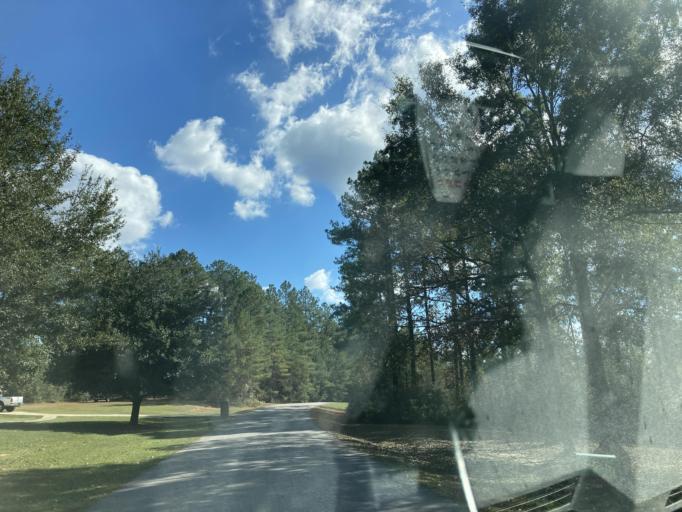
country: US
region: Mississippi
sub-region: Lamar County
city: Sumrall
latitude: 31.3641
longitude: -89.5113
